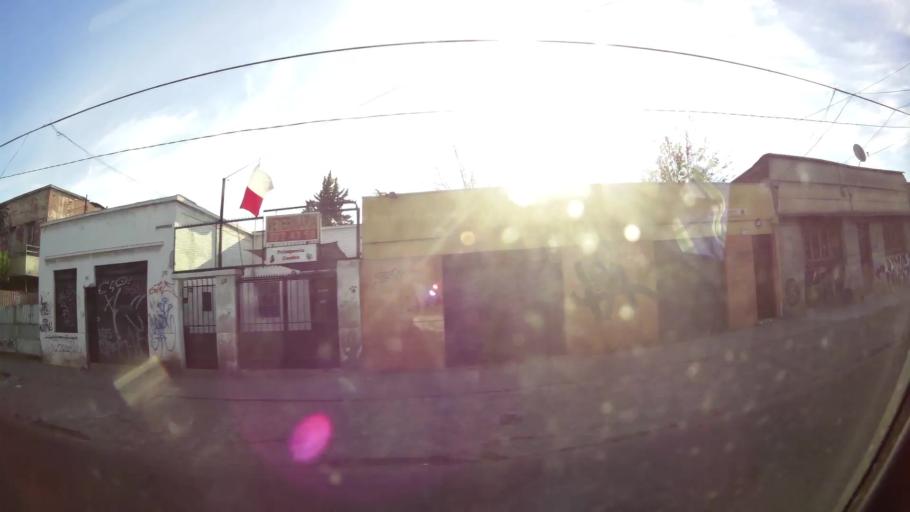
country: CL
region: Santiago Metropolitan
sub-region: Provincia de Santiago
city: Lo Prado
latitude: -33.4443
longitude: -70.7074
